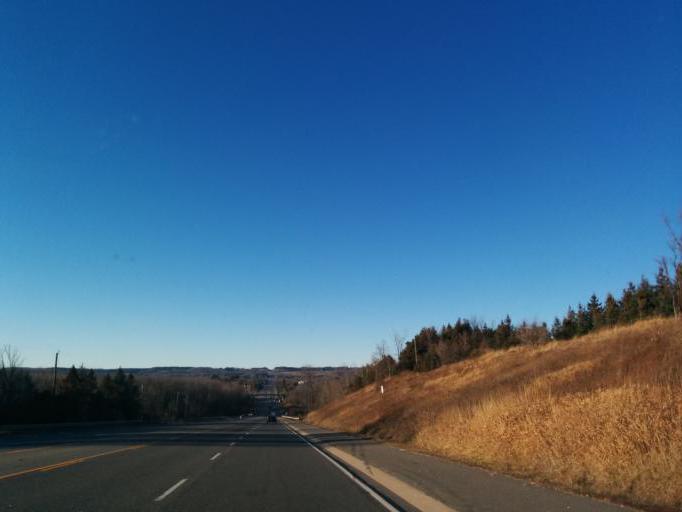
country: CA
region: Ontario
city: Brampton
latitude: 43.8073
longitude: -79.9242
